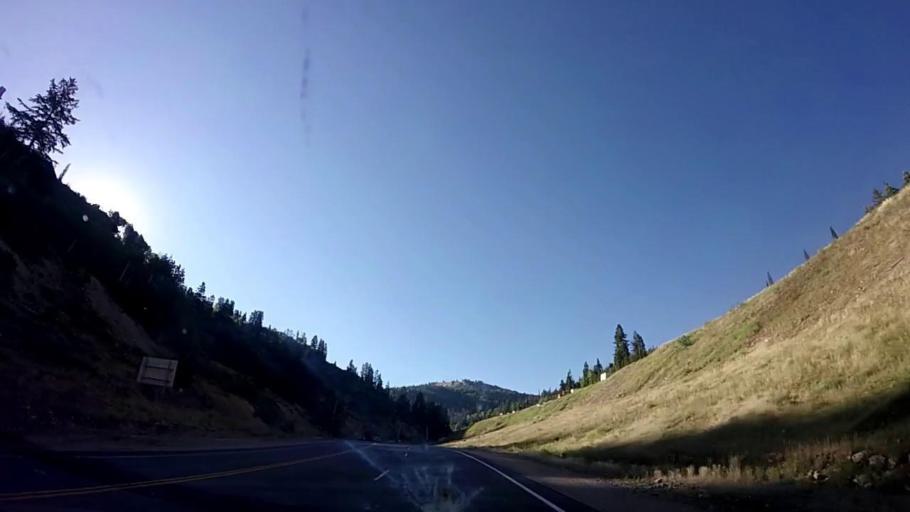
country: US
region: Utah
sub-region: Summit County
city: Park City
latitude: 40.6242
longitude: -111.4961
